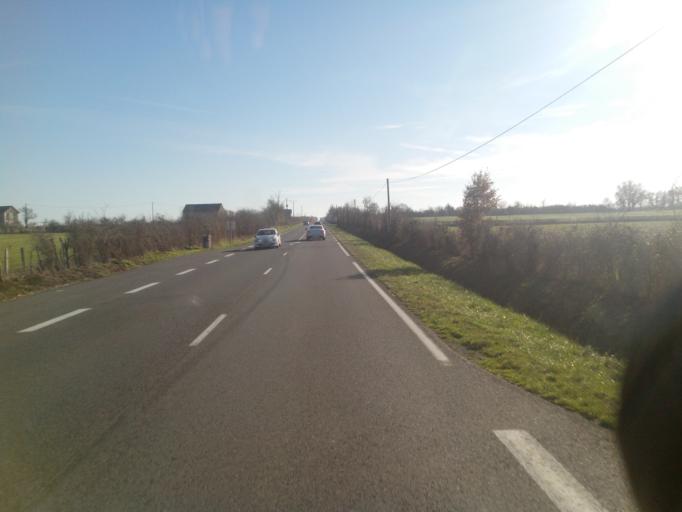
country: FR
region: Poitou-Charentes
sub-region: Departement de la Vienne
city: Lussac-les-Chateaux
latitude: 46.3710
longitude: 0.7631
